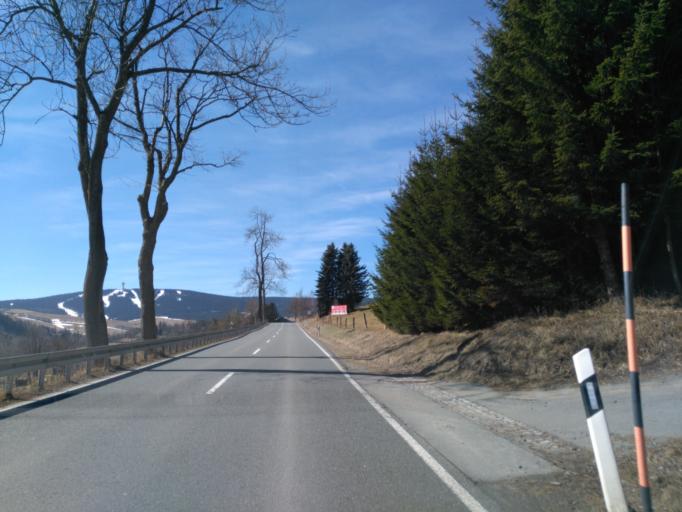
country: DE
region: Saxony
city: Kurort Oberwiesenthal
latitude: 50.4327
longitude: 12.9932
